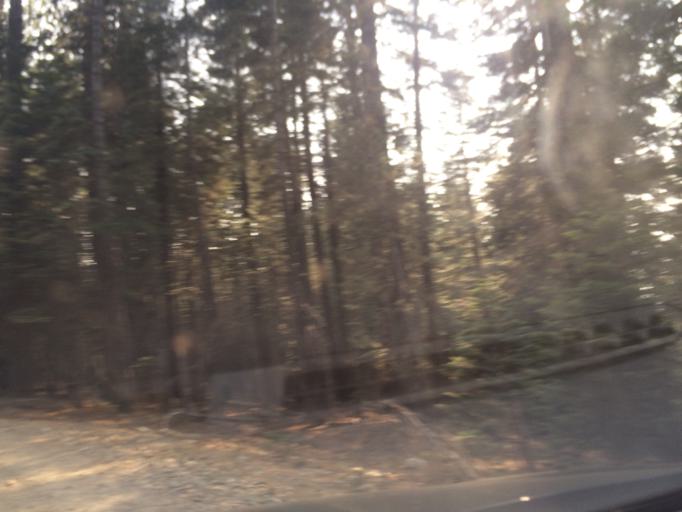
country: US
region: California
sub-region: Sierra County
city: Downieville
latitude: 39.3925
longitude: -120.6659
